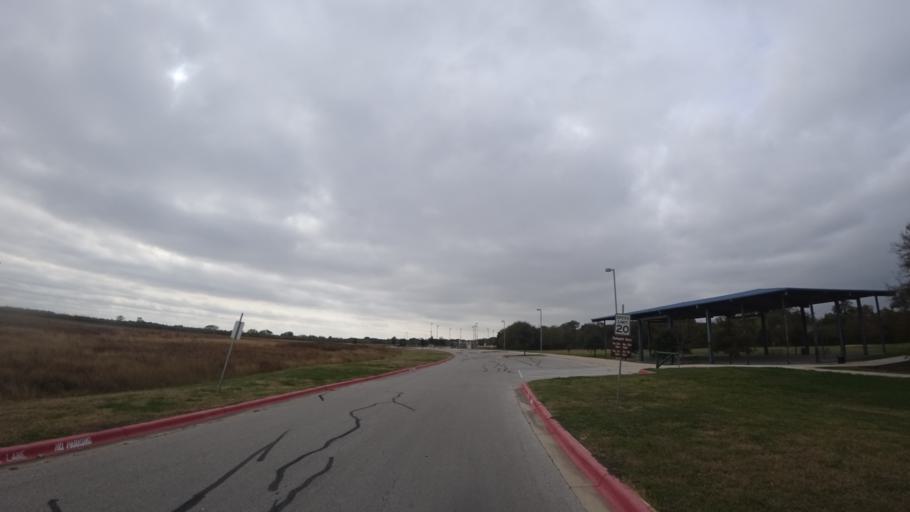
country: US
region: Texas
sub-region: Travis County
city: Pflugerville
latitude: 30.4082
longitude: -97.5972
